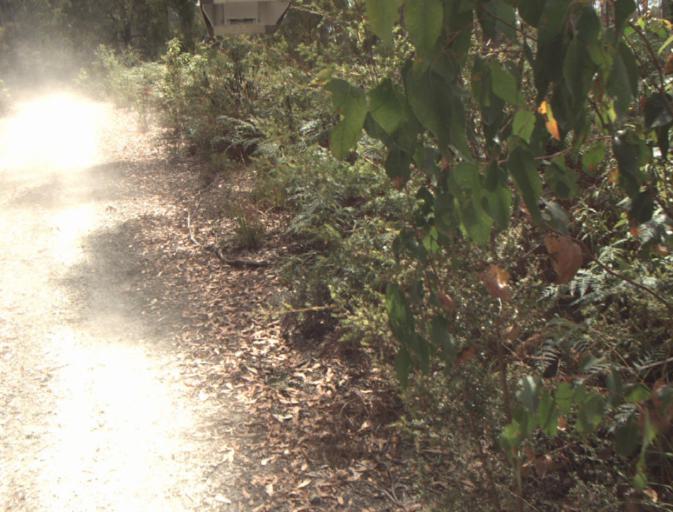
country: AU
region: Tasmania
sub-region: Launceston
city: Mayfield
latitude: -41.2019
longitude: 147.1637
